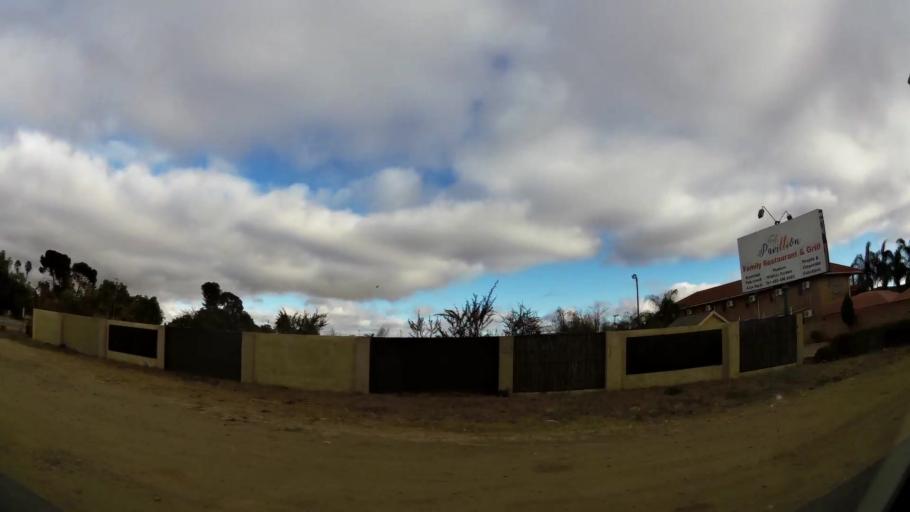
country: ZA
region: Limpopo
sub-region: Capricorn District Municipality
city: Polokwane
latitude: -23.9274
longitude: 29.4512
